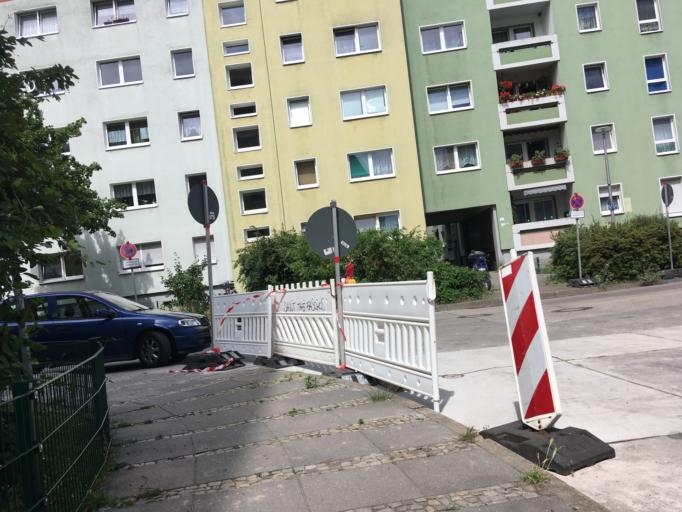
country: DE
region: Berlin
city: Kopenick Bezirk
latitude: 52.4379
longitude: 13.5660
